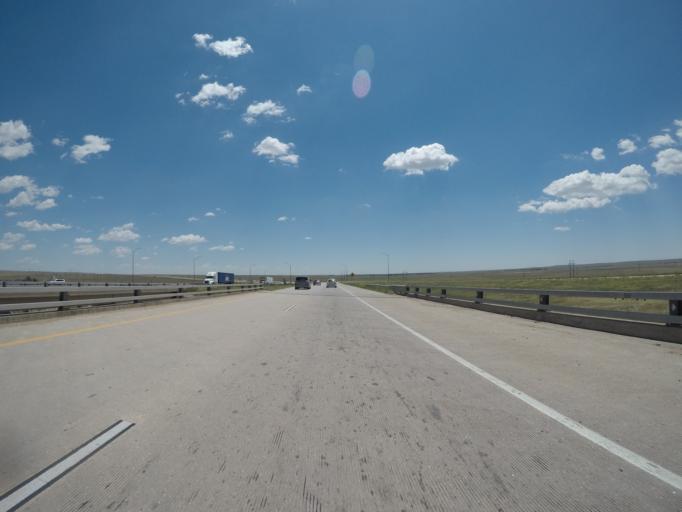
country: US
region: Colorado
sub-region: Lincoln County
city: Limon
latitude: 39.2635
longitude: -103.6665
